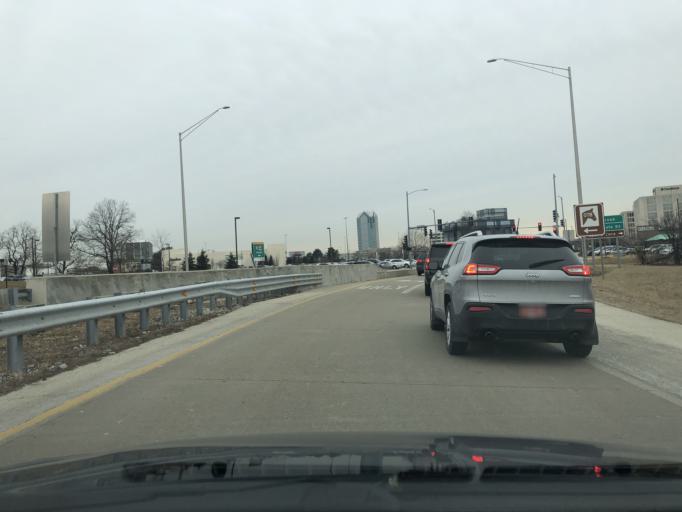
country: US
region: Illinois
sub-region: DuPage County
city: Oakbrook Terrace
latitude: 41.8460
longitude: -87.9479
